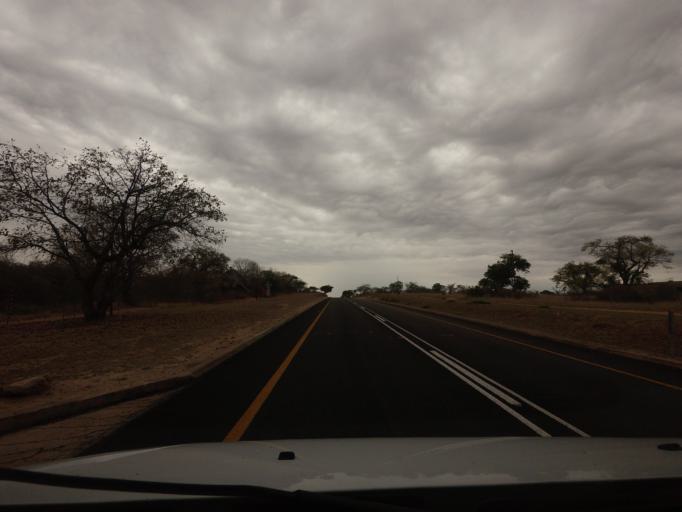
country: ZA
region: Limpopo
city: Thulamahashi
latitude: -24.5662
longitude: 31.1078
